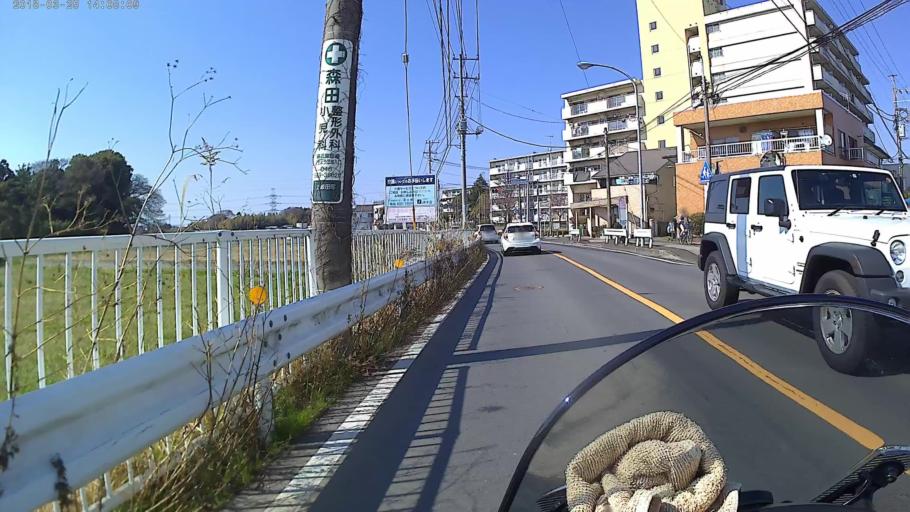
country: JP
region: Kanagawa
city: Minami-rinkan
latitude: 35.4198
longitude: 139.4790
